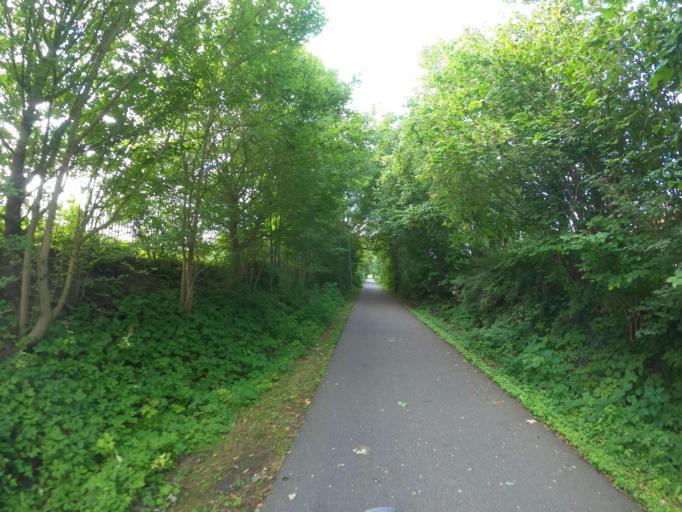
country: SE
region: Skane
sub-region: Lunds Kommun
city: Lund
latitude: 55.6854
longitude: 13.1894
